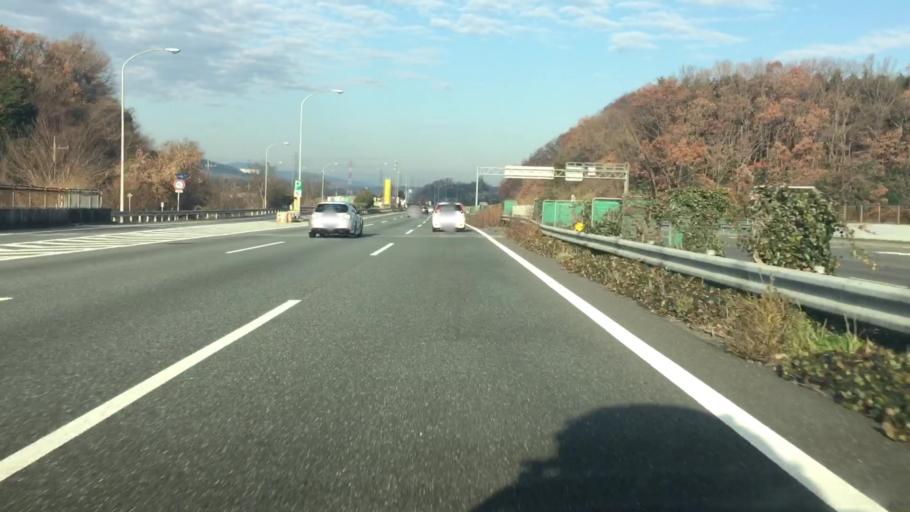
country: JP
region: Saitama
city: Ogawa
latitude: 36.0848
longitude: 139.2941
